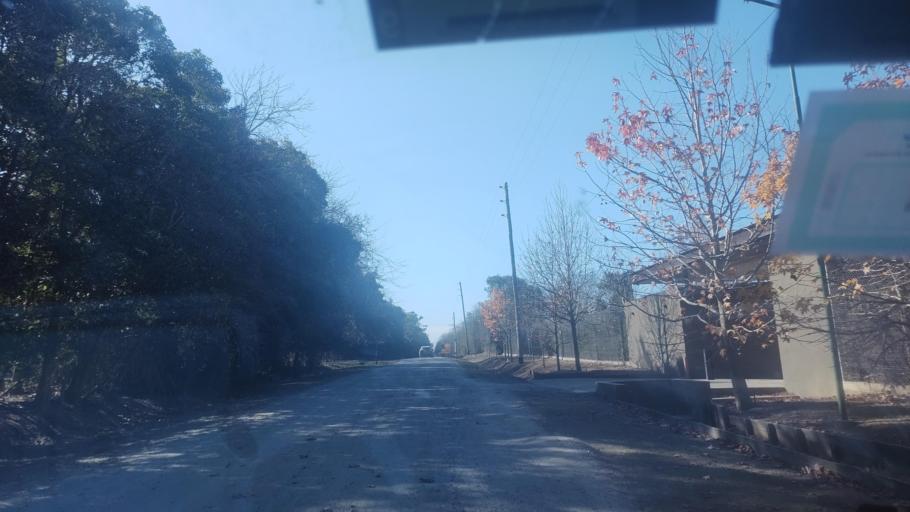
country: AR
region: Buenos Aires
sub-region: Partido de La Plata
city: La Plata
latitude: -34.8565
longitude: -58.1099
